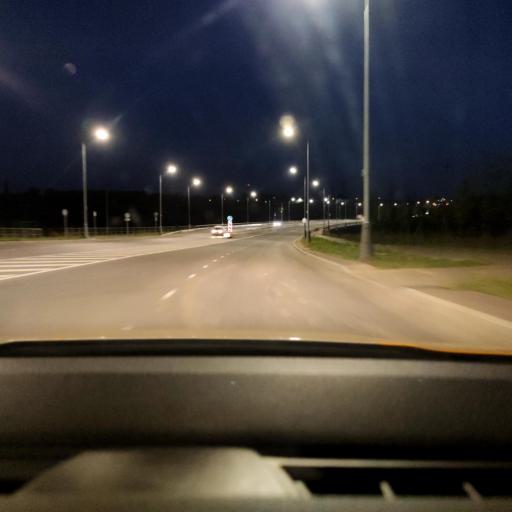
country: RU
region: Moskovskaya
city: Shcherbinka
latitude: 55.4924
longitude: 37.5217
